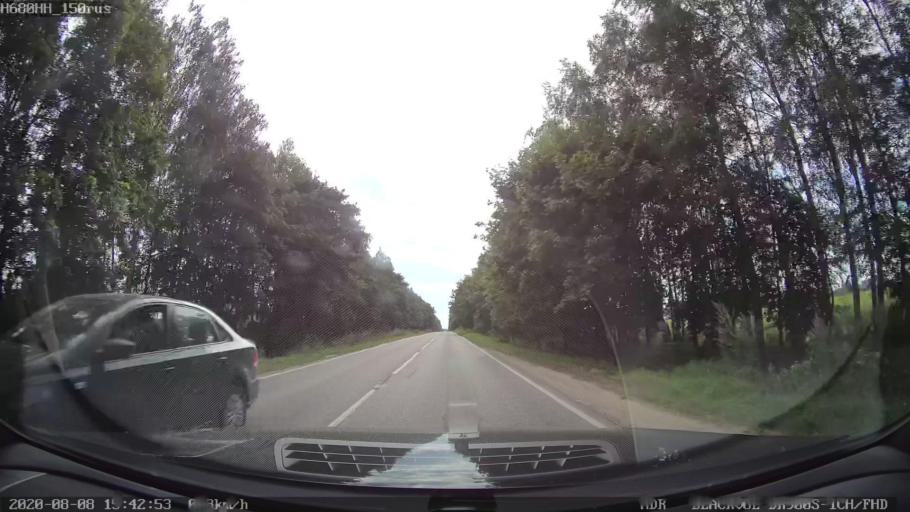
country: RU
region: Tula
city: Zaokskiy
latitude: 54.7353
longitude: 37.3512
